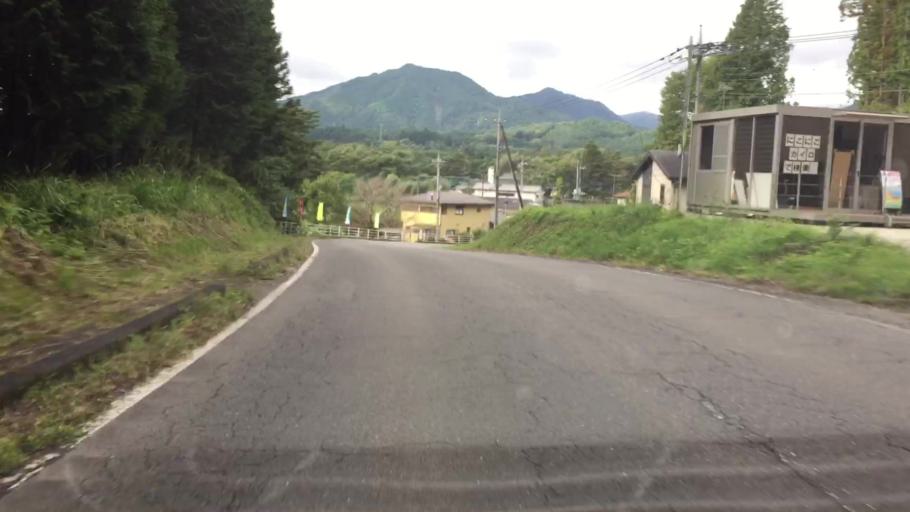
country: JP
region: Tochigi
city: Nikko
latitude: 36.7466
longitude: 139.6537
